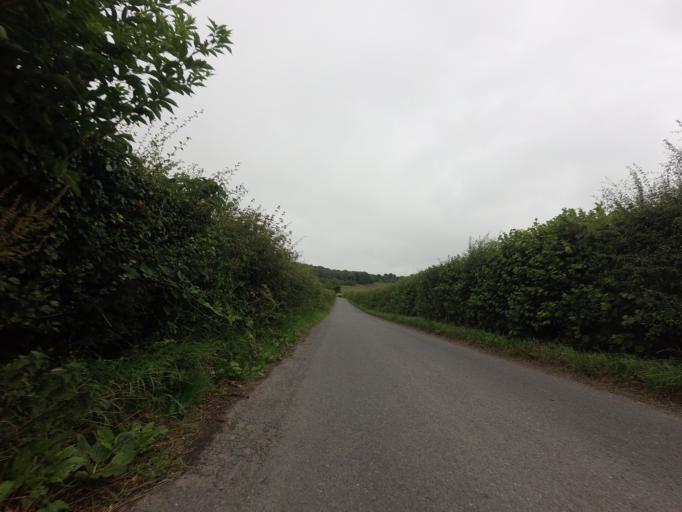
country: GB
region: England
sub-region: Kent
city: Borough Green
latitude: 51.3098
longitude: 0.2695
